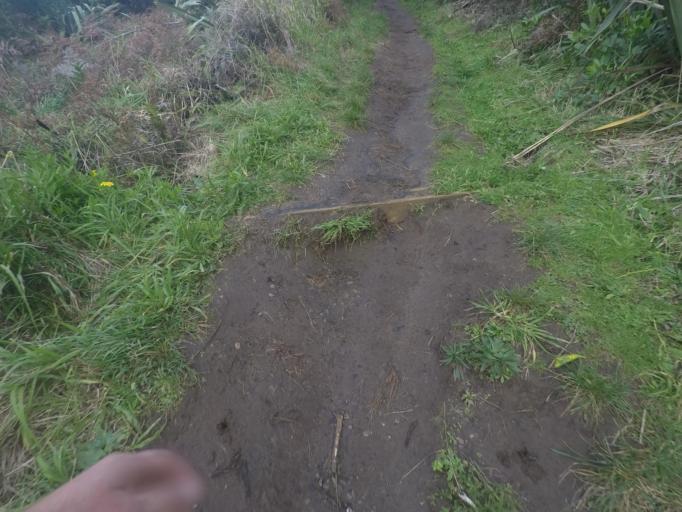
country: NZ
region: Auckland
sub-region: Auckland
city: Muriwai Beach
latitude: -36.8889
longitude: 174.4464
